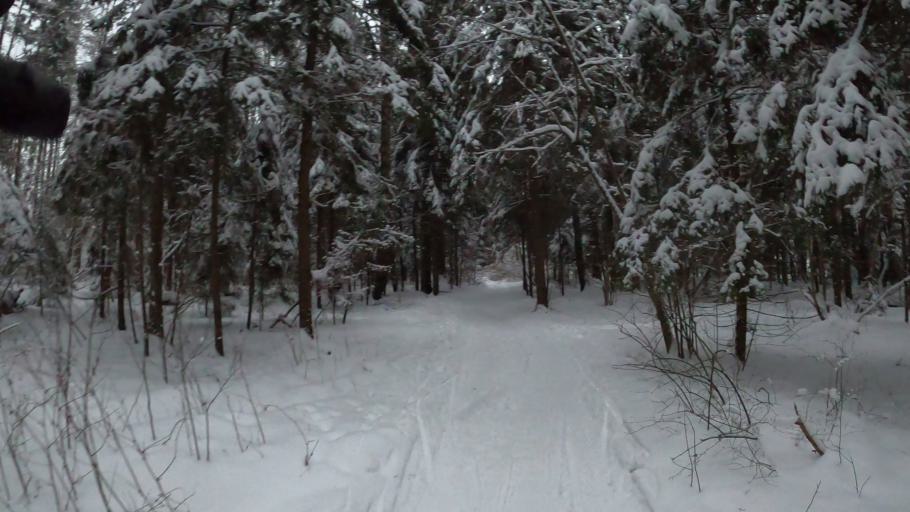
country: RU
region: Moskovskaya
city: Firsanovka
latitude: 55.9071
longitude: 37.2038
